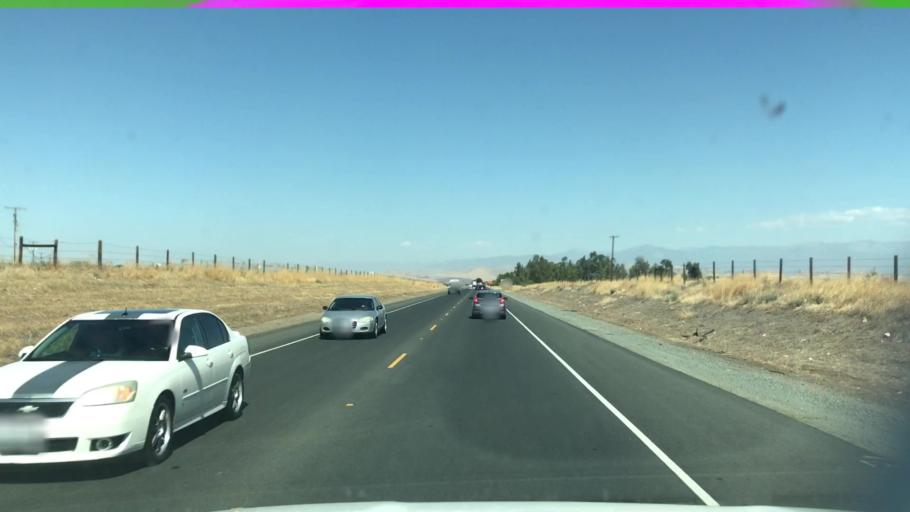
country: US
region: California
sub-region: Tulare County
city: Terra Bella
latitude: 35.9953
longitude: -119.0453
